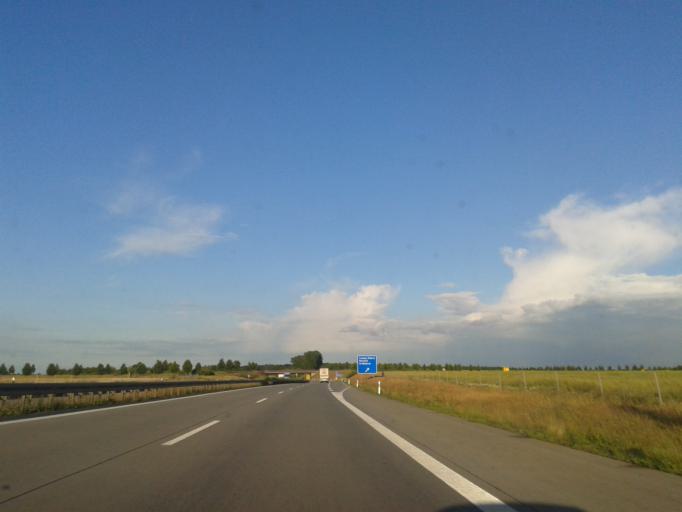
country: DE
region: Saxony
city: Grossposna
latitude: 51.2628
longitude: 12.4585
